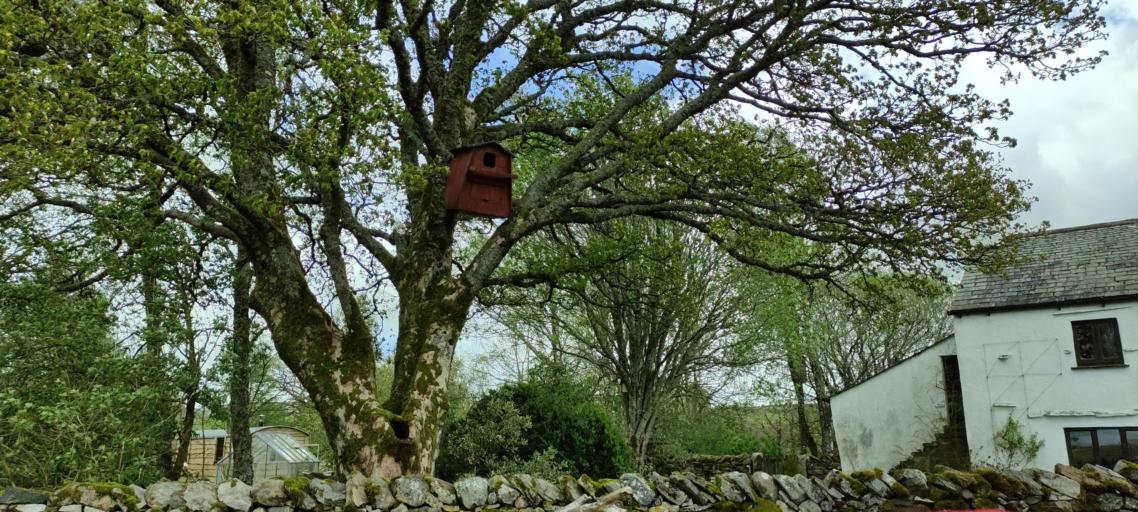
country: GB
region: England
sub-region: Cumbria
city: Penrith
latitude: 54.5158
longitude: -2.6815
